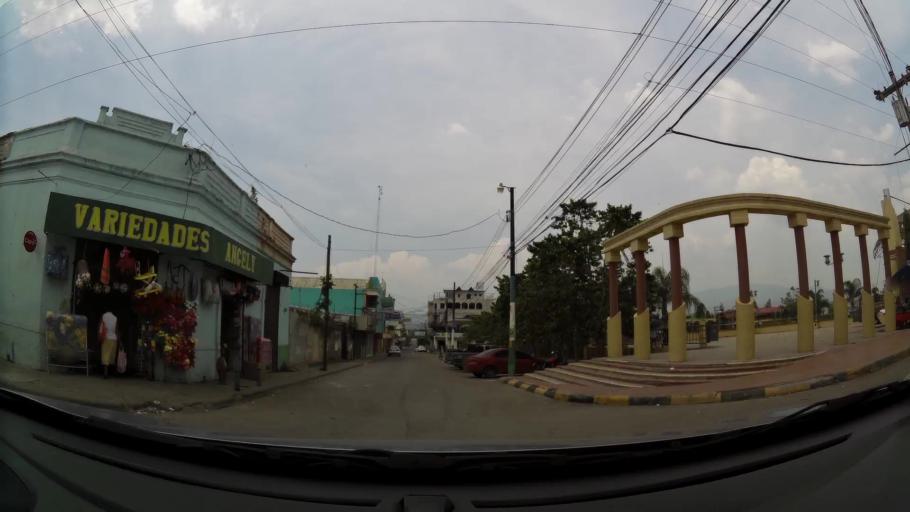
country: HN
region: Comayagua
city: Siguatepeque
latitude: 14.5973
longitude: -87.8306
